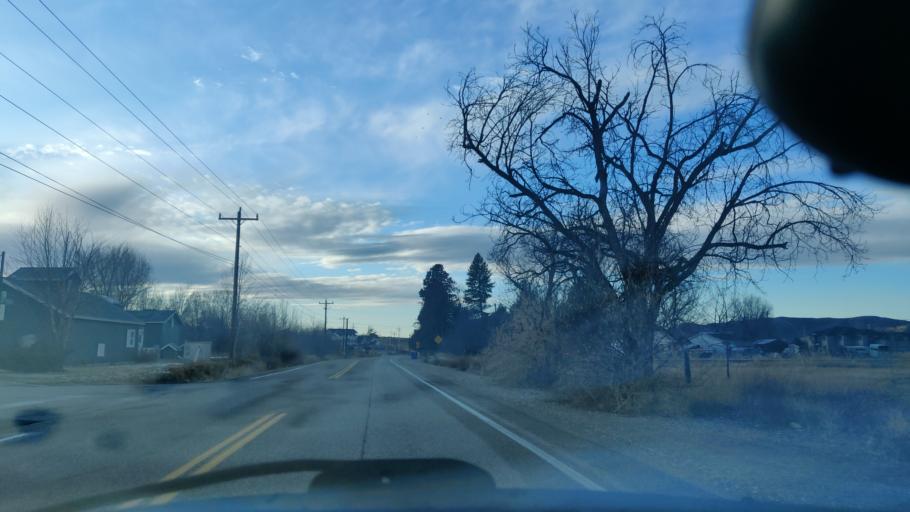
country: US
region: Idaho
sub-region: Ada County
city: Eagle
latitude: 43.7278
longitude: -116.2565
